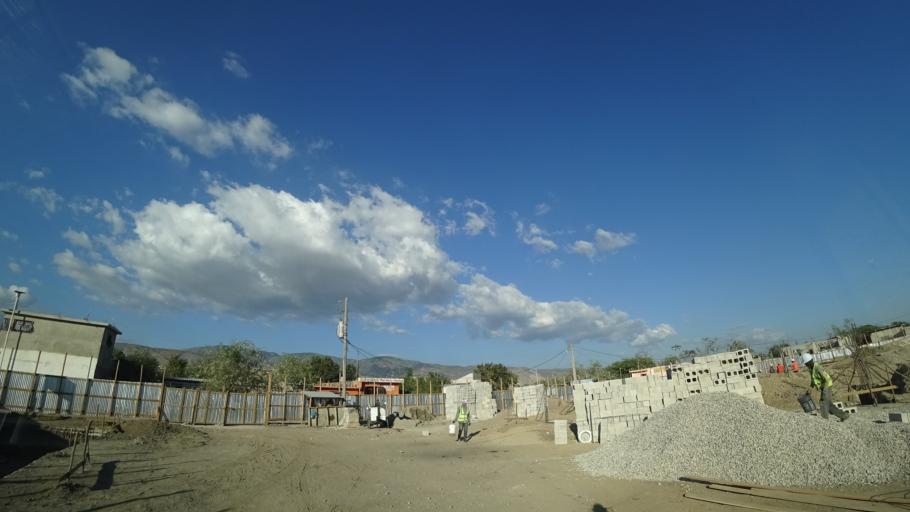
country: HT
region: Ouest
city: Croix des Bouquets
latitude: 18.6460
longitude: -72.2728
